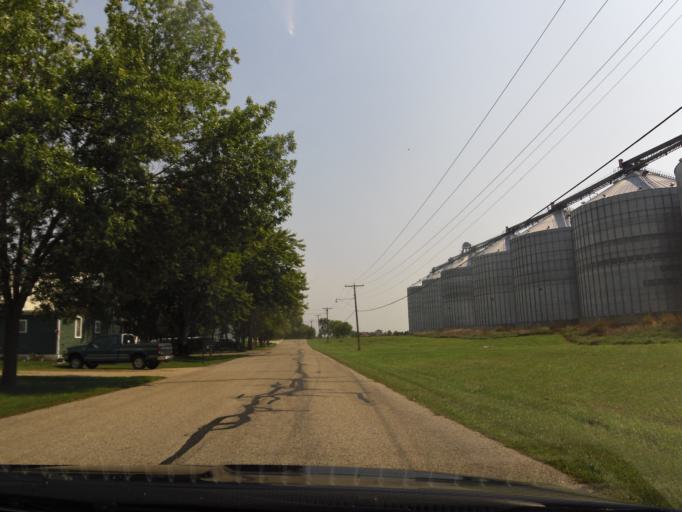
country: US
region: South Dakota
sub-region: Roberts County
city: Sisseton
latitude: 46.0723
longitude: -97.1469
